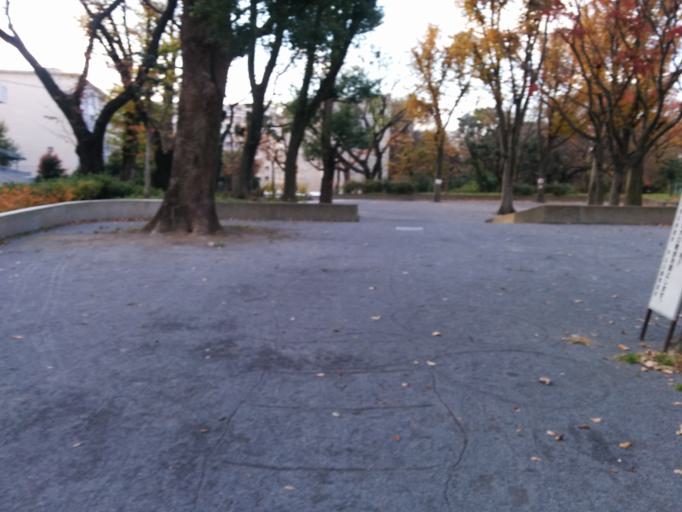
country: JP
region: Tokyo
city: Tokyo
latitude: 35.7024
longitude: 139.7146
